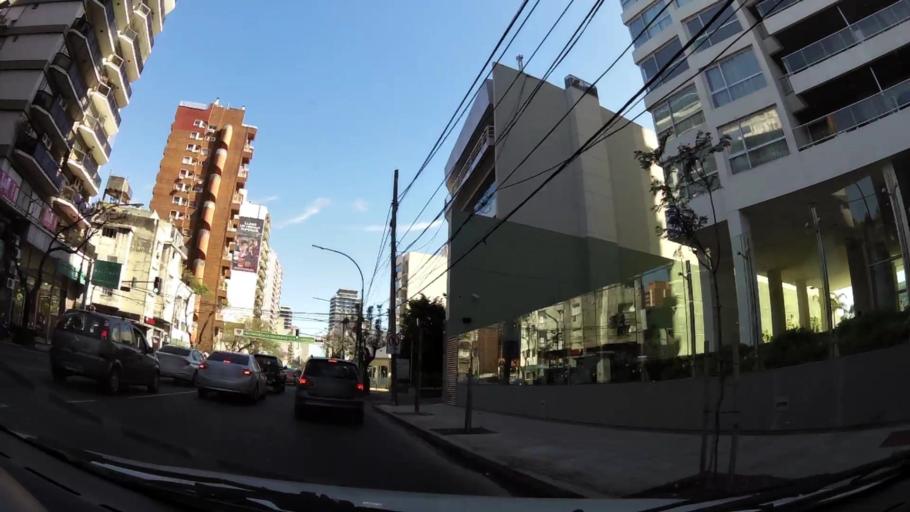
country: AR
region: Buenos Aires
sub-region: Partido de Vicente Lopez
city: Olivos
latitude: -34.5218
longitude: -58.4735
